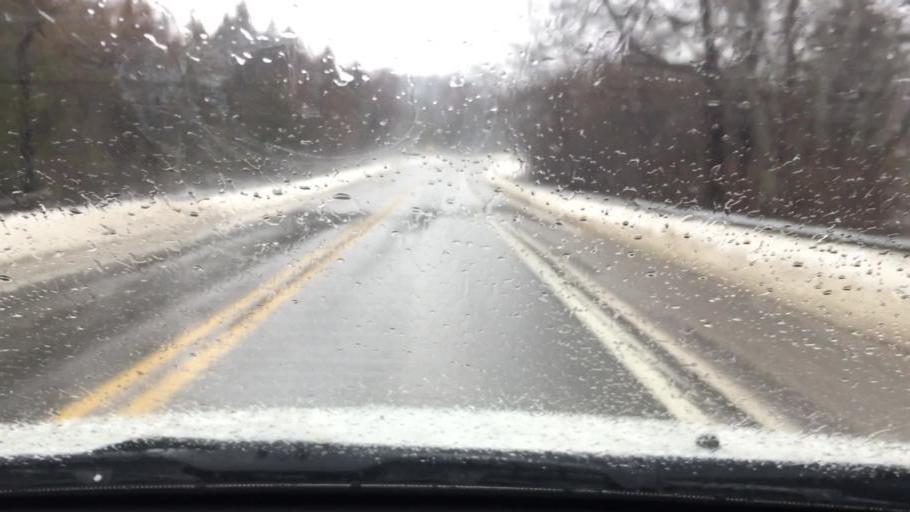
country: US
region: Michigan
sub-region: Charlevoix County
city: Charlevoix
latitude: 45.2494
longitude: -85.1820
